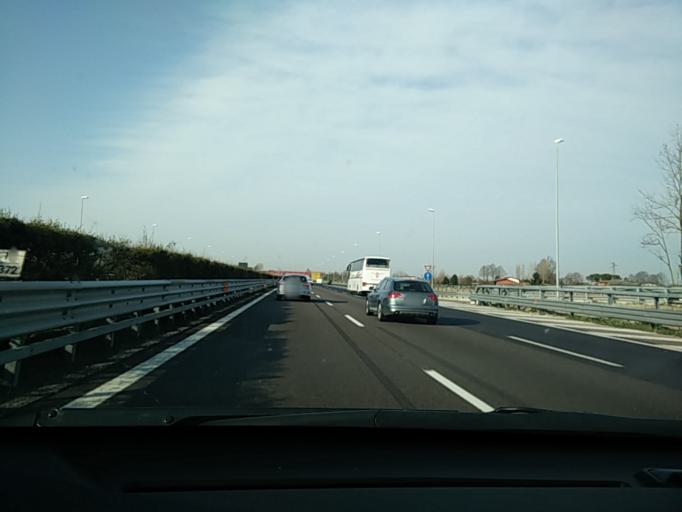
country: IT
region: Veneto
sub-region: Provincia di Venezia
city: Arino
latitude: 45.4415
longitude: 12.0511
